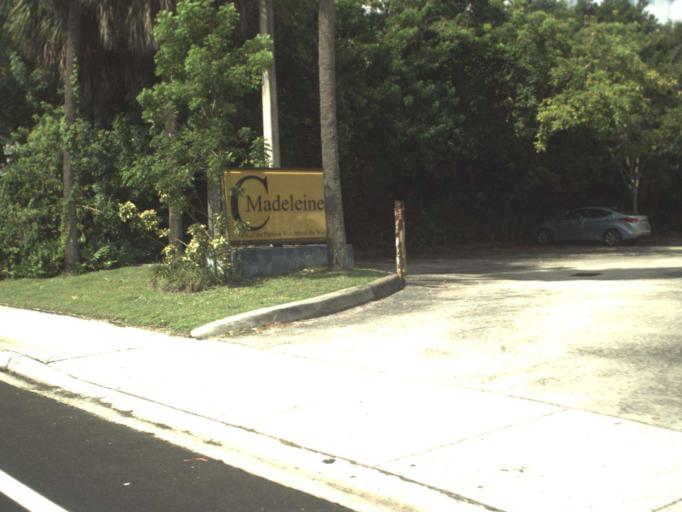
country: US
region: Florida
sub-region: Miami-Dade County
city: Biscayne Park
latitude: 25.9025
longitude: -80.1599
